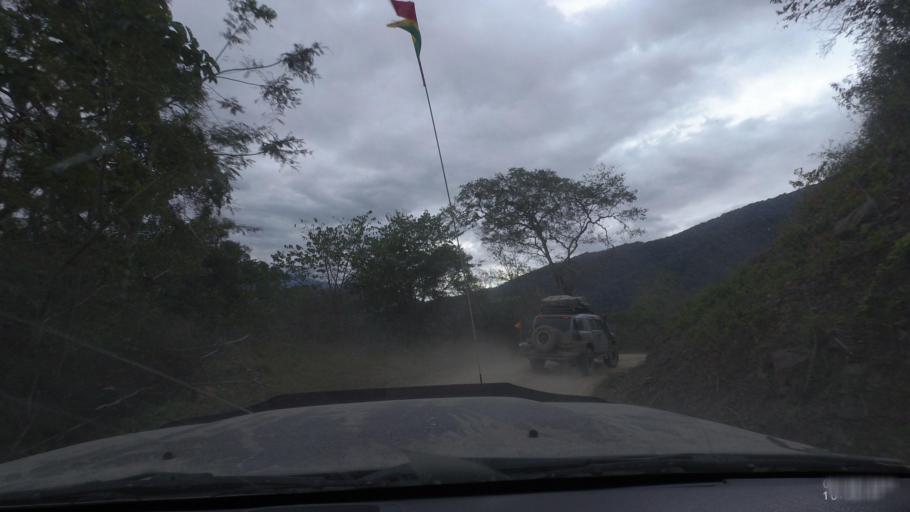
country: BO
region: La Paz
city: Quime
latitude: -16.5114
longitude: -66.7631
